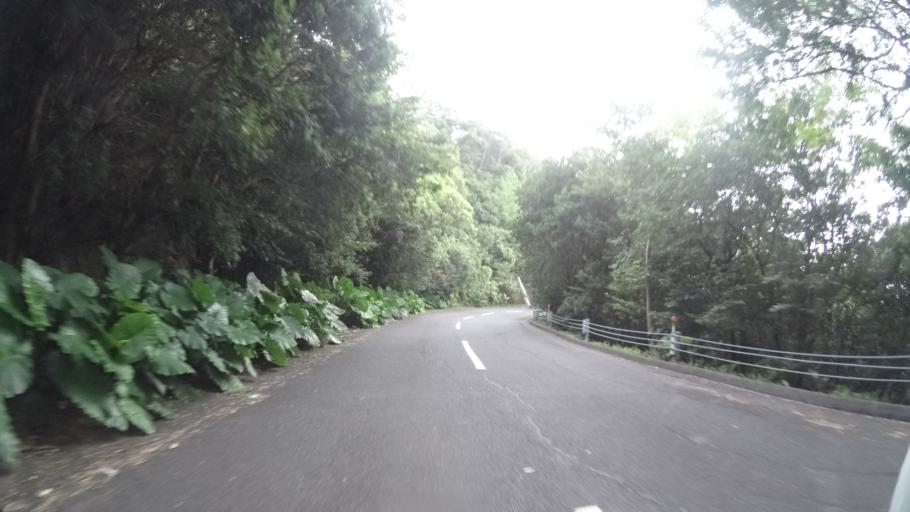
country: JP
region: Kagoshima
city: Nishinoomote
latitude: 30.3246
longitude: 130.3960
